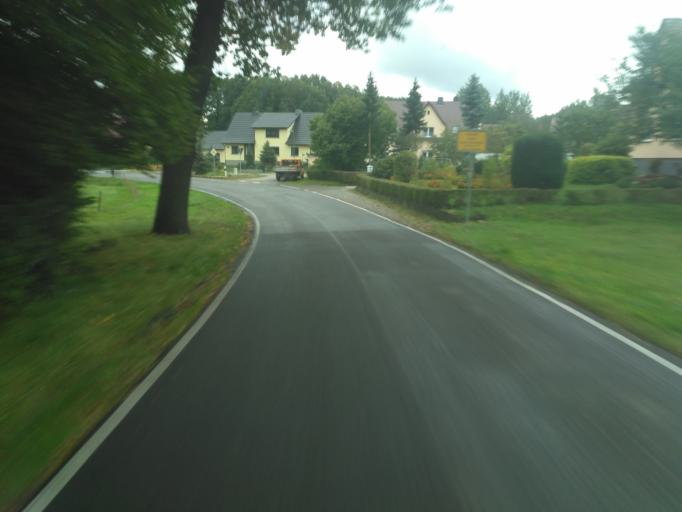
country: DE
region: Saxony
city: Wittichenau
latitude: 51.3669
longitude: 14.2601
